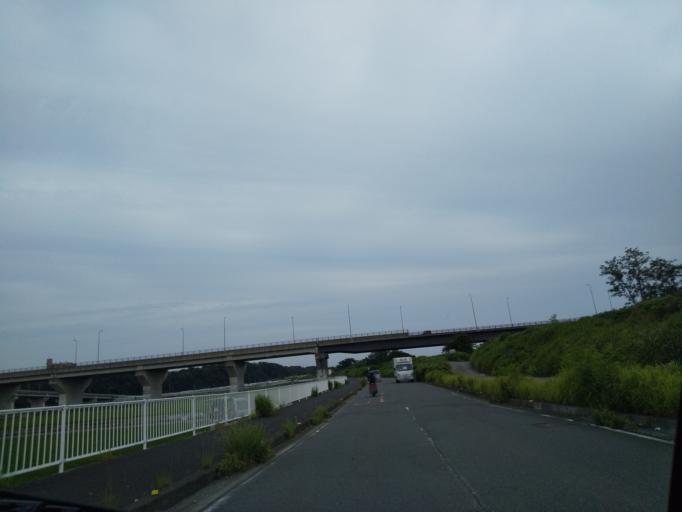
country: JP
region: Kanagawa
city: Zama
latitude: 35.4863
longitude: 139.3567
